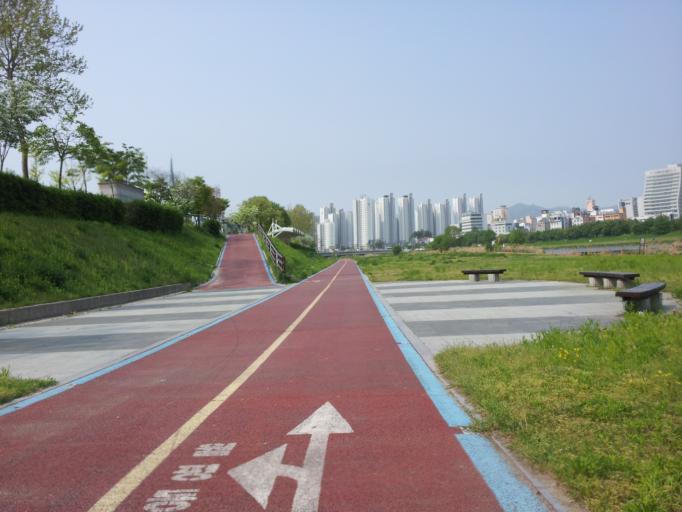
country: KR
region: Daejeon
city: Daejeon
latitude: 36.3555
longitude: 127.3551
